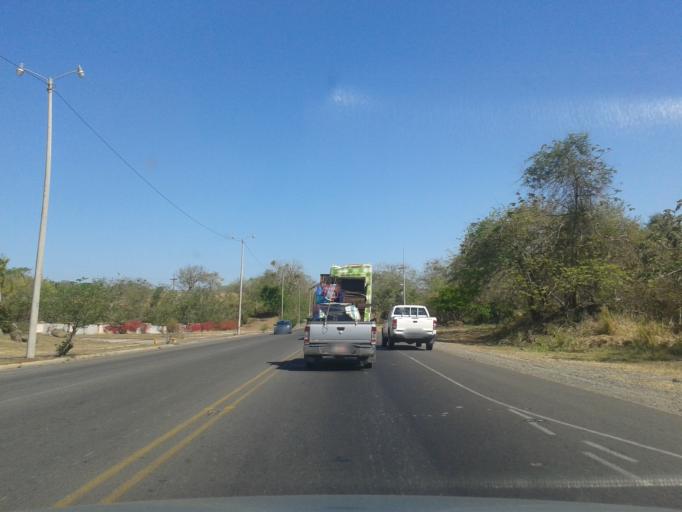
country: CR
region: Puntarenas
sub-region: Canton Central de Puntarenas
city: Chacarita
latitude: 9.9462
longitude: -84.7277
